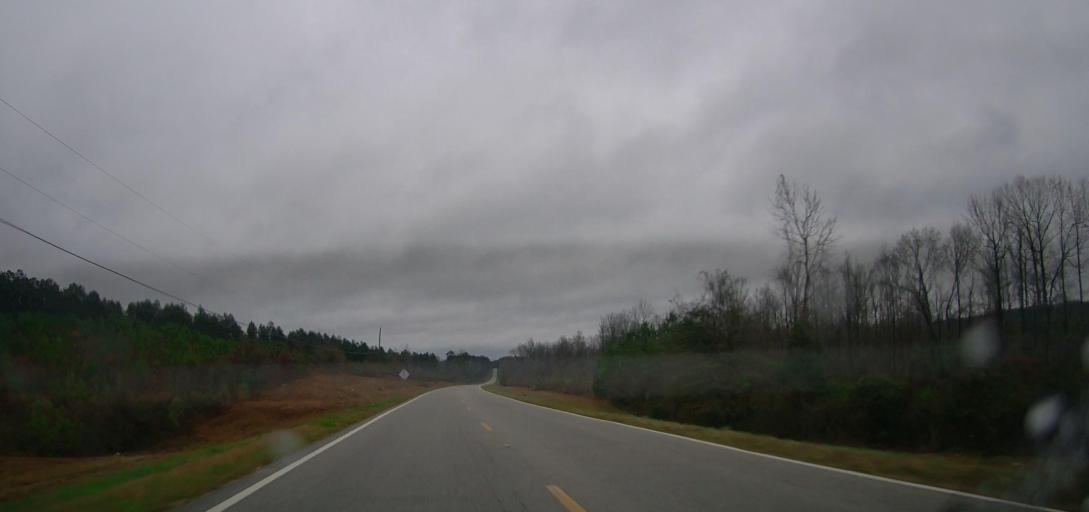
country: US
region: Alabama
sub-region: Bibb County
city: Centreville
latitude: 32.8862
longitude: -86.9825
